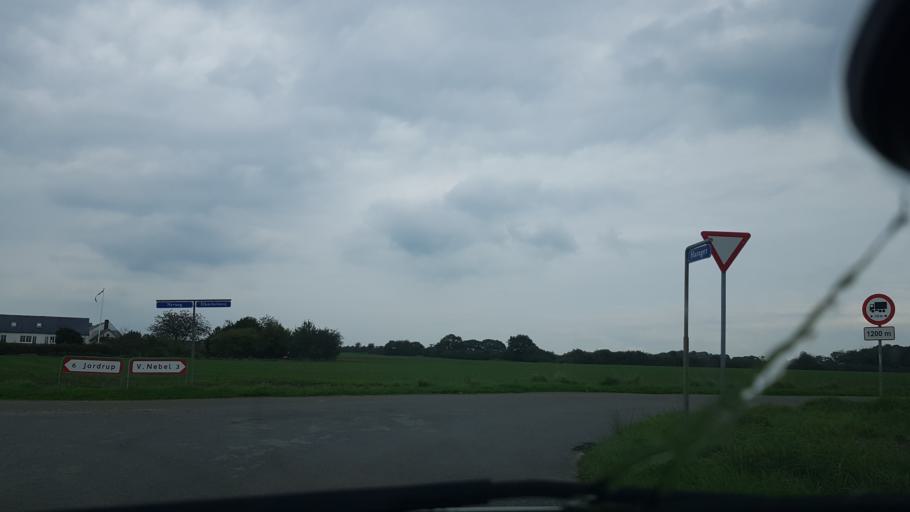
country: DK
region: South Denmark
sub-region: Kolding Kommune
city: Kolding
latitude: 55.5427
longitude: 9.3883
